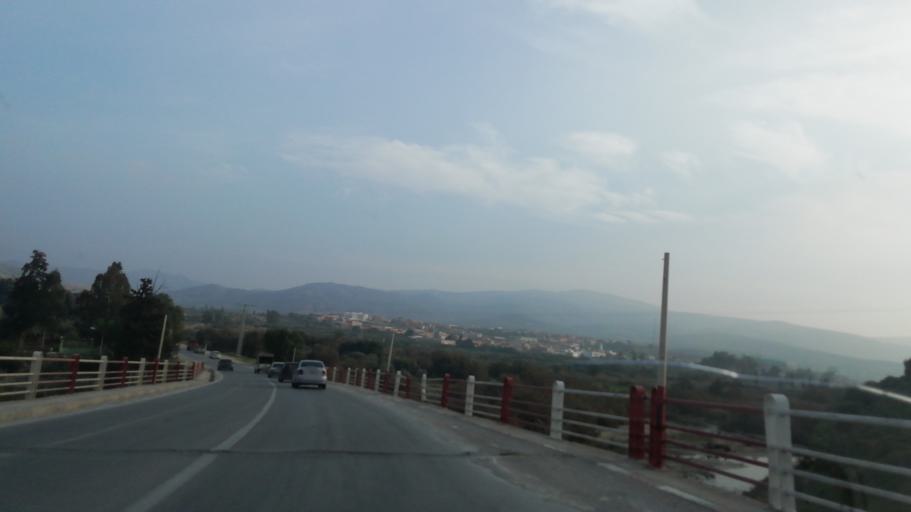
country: DZ
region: Mascara
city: Bou Hanifia el Hamamat
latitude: 35.4689
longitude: -0.0106
